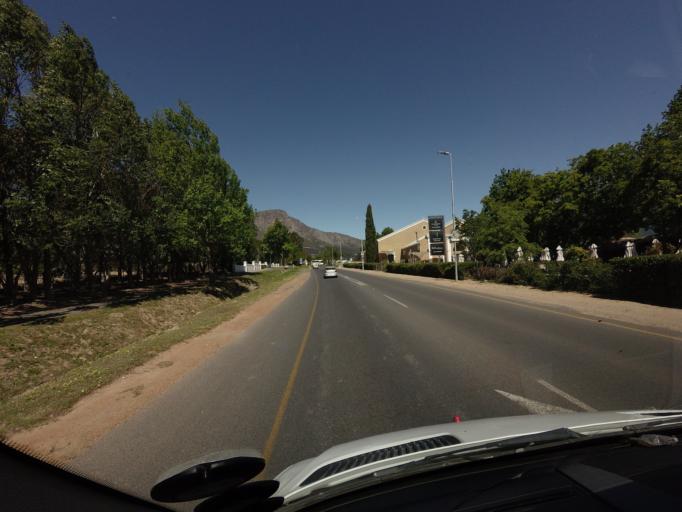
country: ZA
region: Western Cape
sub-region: Cape Winelands District Municipality
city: Paarl
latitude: -33.9047
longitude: 19.1121
